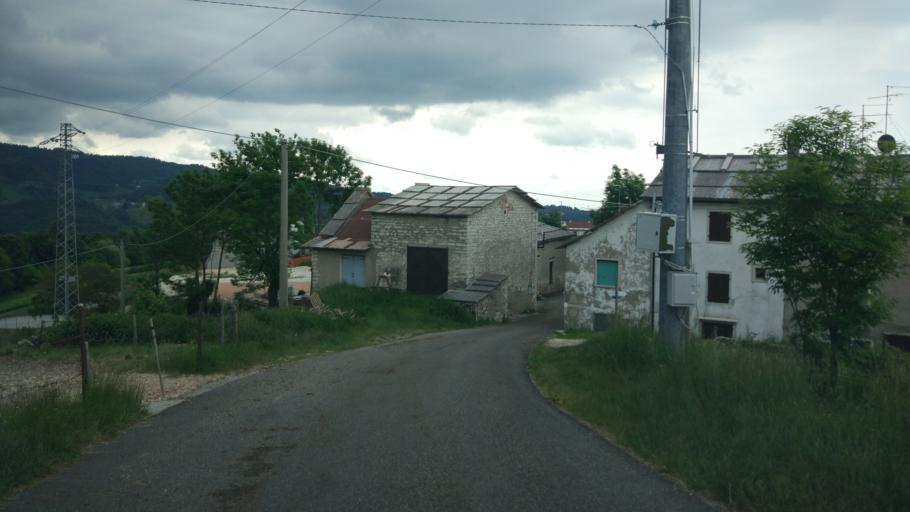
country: IT
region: Veneto
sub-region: Provincia di Verona
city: Erbezzo
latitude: 45.6487
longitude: 10.9995
